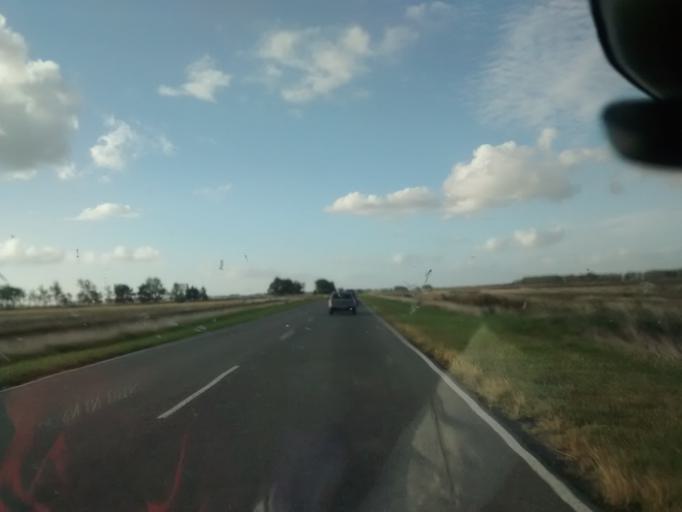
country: AR
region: Buenos Aires
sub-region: Partido de General Belgrano
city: General Belgrano
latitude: -36.1928
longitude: -58.5928
